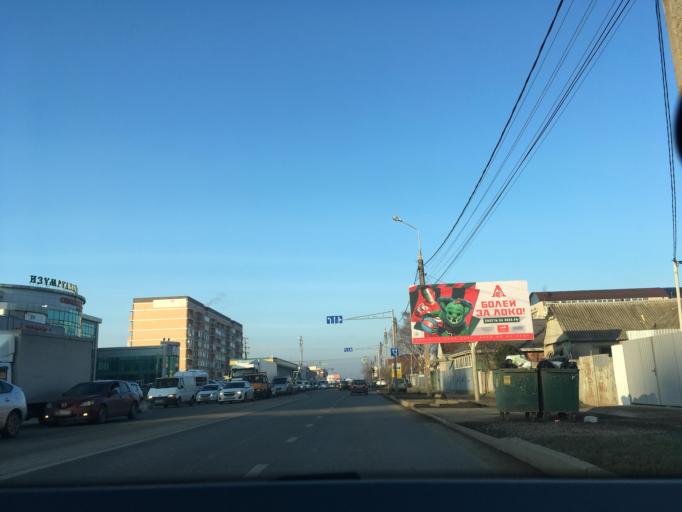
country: RU
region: Krasnodarskiy
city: Krasnodar
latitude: 45.1129
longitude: 39.0122
